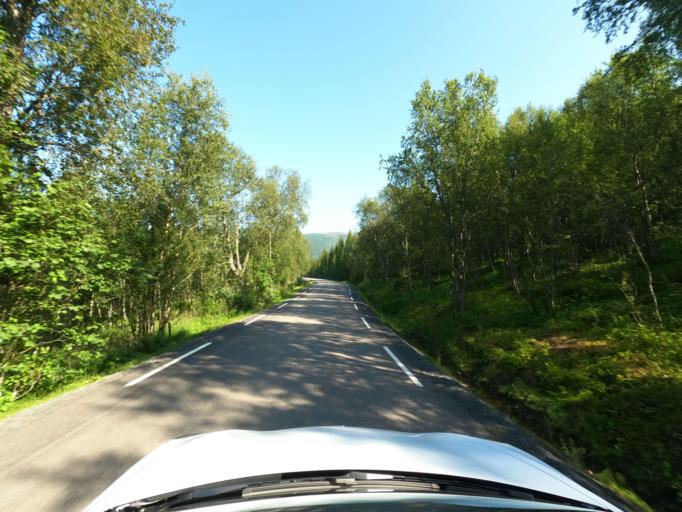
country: NO
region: Nordland
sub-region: Narvik
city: Narvik
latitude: 68.3931
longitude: 17.3134
